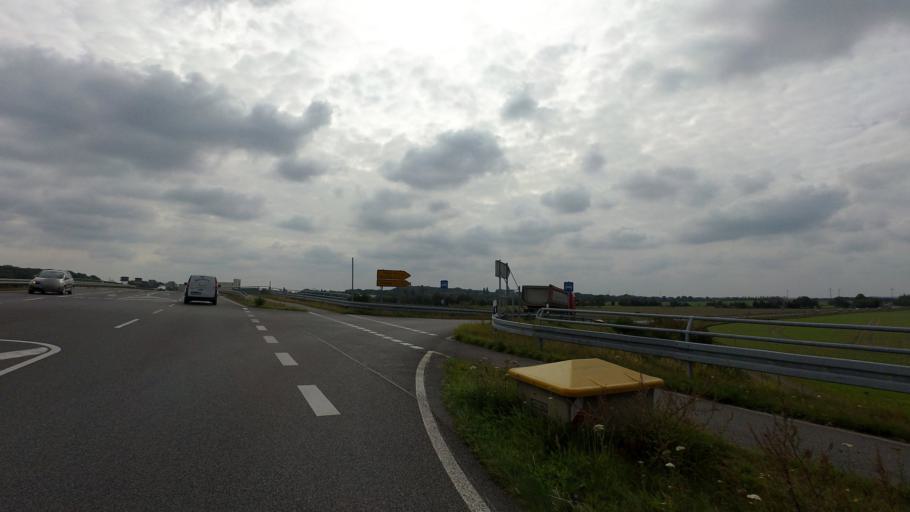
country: DE
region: Brandenburg
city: Luckau
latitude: 51.8652
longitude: 13.7020
